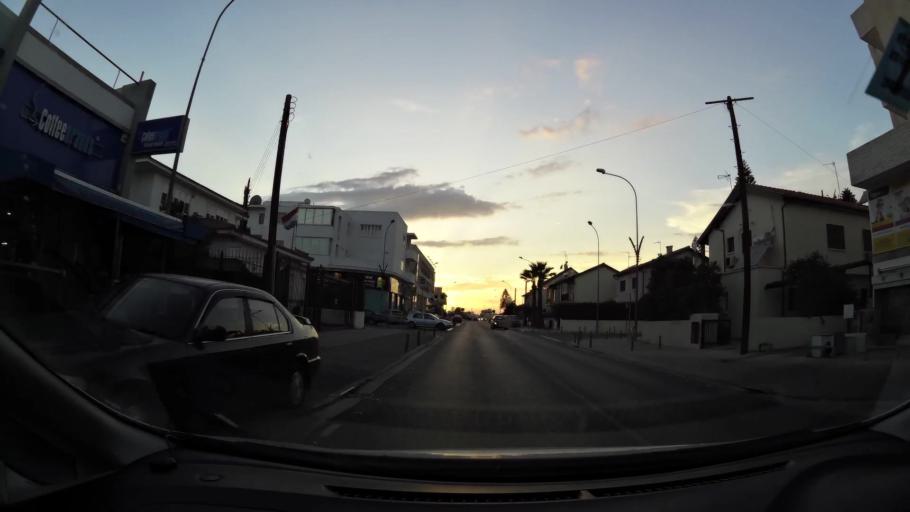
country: CY
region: Lefkosia
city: Nicosia
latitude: 35.1487
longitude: 33.3858
